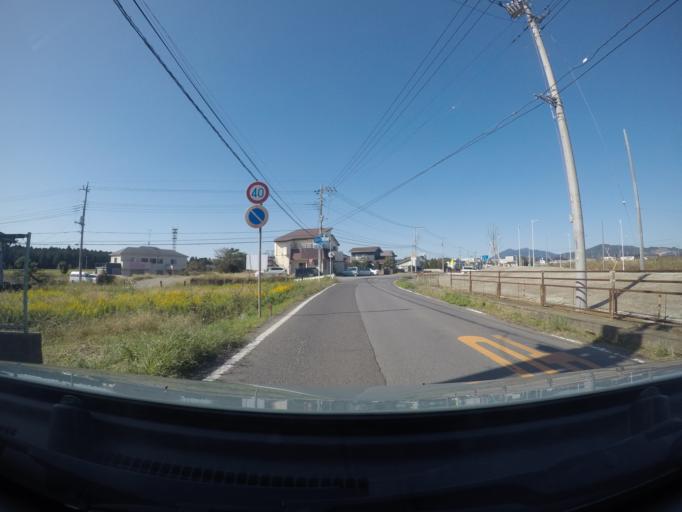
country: JP
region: Ibaraki
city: Naka
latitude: 36.1088
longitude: 140.1200
